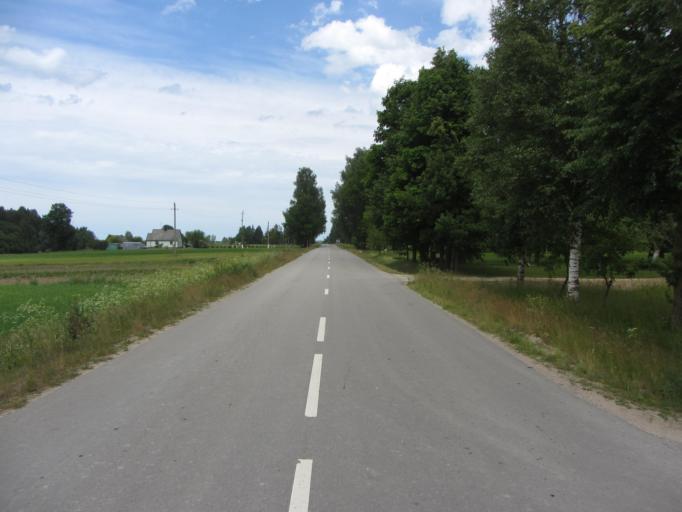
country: LT
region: Panevezys
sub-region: Birzai
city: Birzai
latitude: 56.1777
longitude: 24.9372
